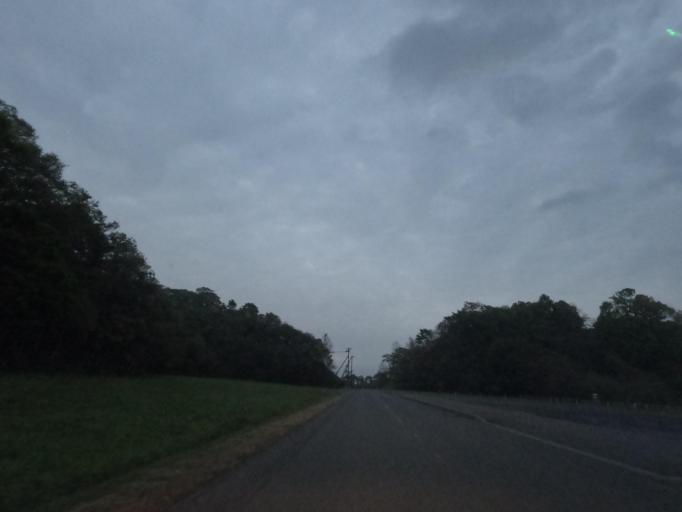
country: JP
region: Hokkaido
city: Date
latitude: 42.5583
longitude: 140.7960
